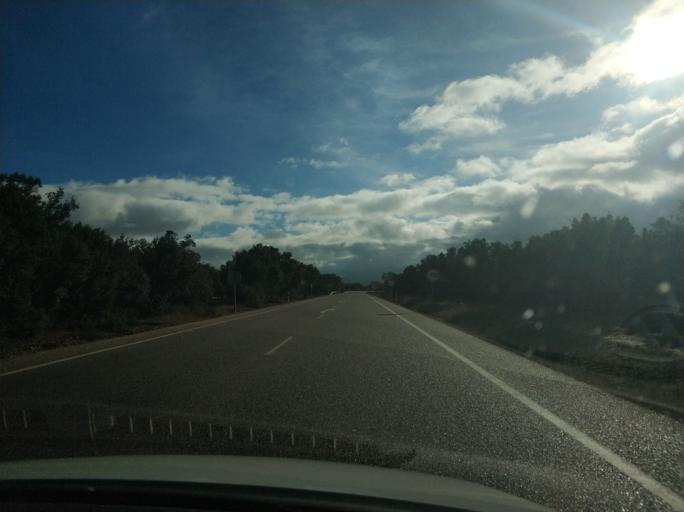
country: ES
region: Castille and Leon
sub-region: Provincia de Segovia
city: Ribota
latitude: 41.3895
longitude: -3.4281
